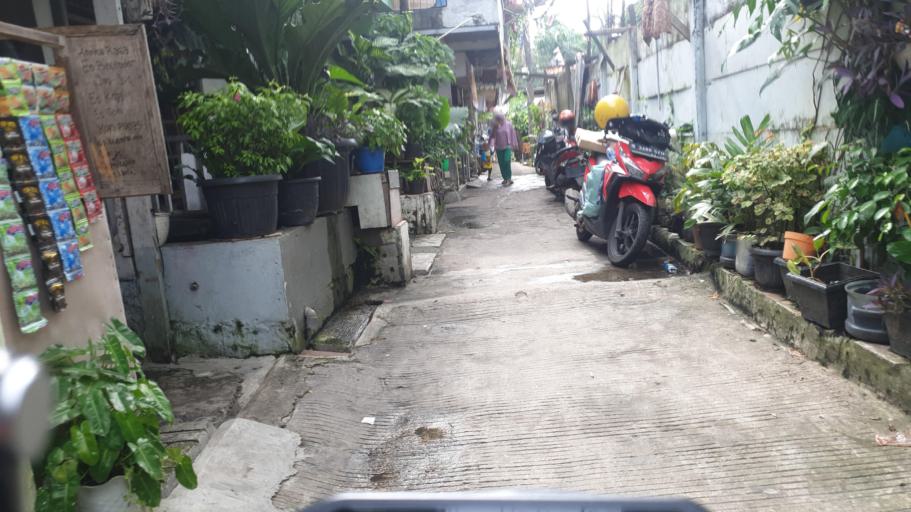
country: ID
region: West Java
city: Pamulang
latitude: -6.2936
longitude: 106.7928
